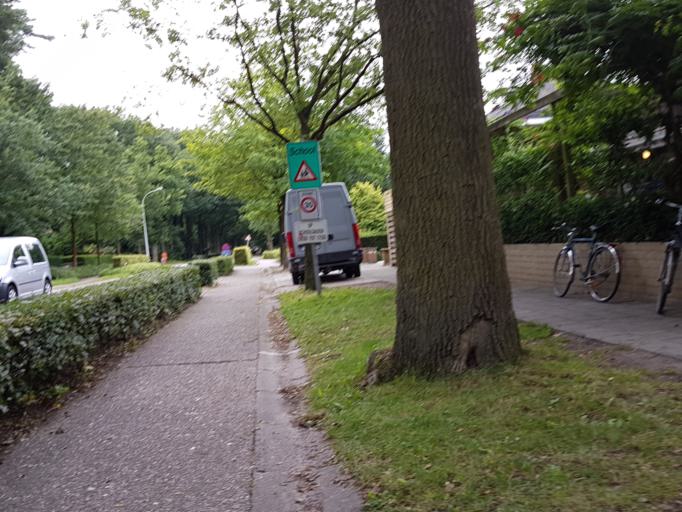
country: BE
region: Flanders
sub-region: Provincie Antwerpen
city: Kalmthout
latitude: 51.3653
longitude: 4.4579
